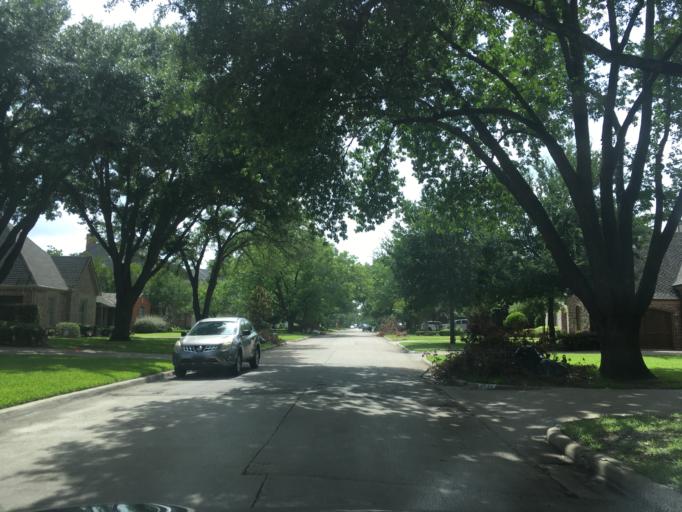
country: US
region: Texas
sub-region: Dallas County
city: University Park
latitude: 32.8832
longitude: -96.7885
